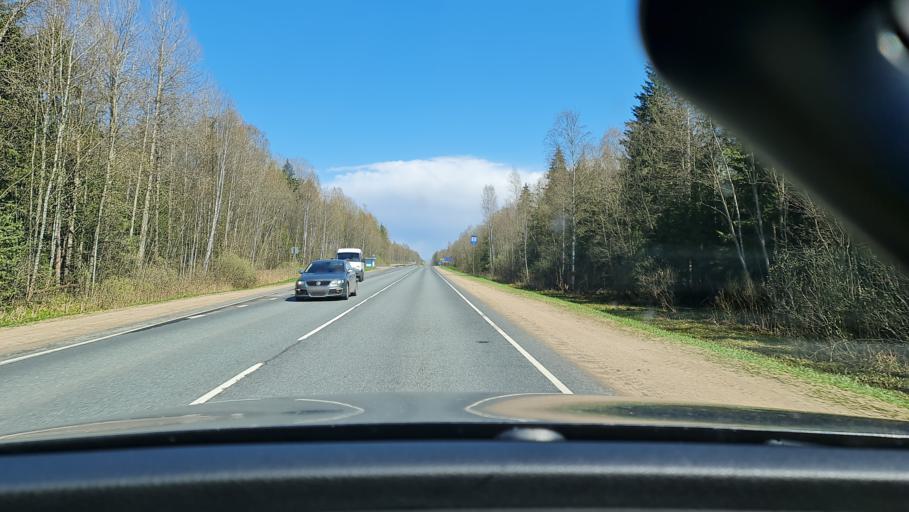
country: RU
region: Tverskaya
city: Rzhev
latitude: 56.2109
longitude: 34.1050
